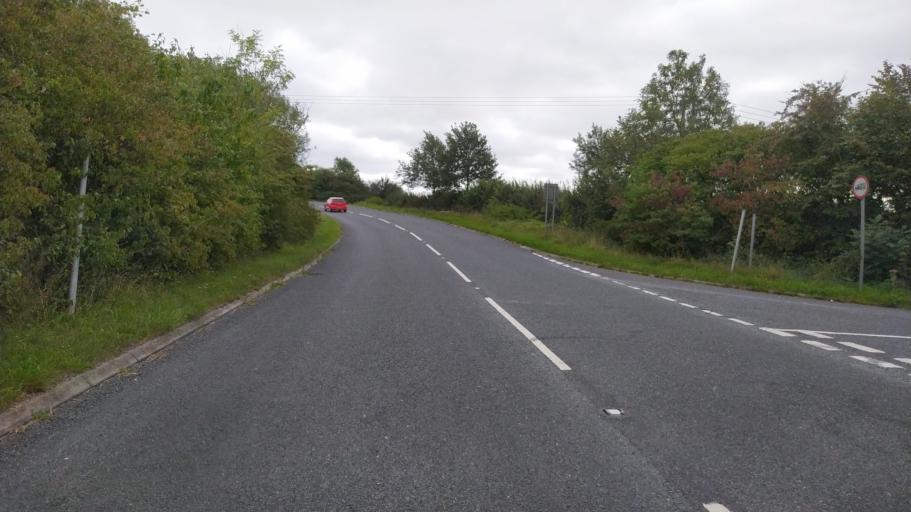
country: GB
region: England
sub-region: Somerset
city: Wincanton
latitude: 51.0678
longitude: -2.3566
